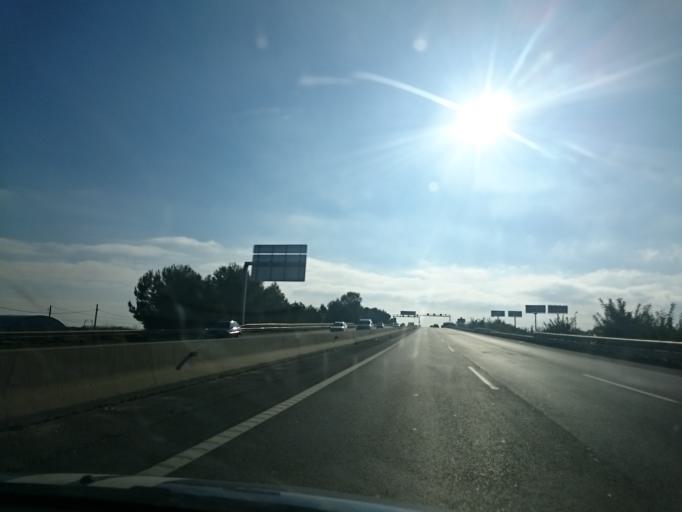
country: ES
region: Catalonia
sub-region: Provincia de Barcelona
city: Viladecans
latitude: 41.3140
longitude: 2.0332
